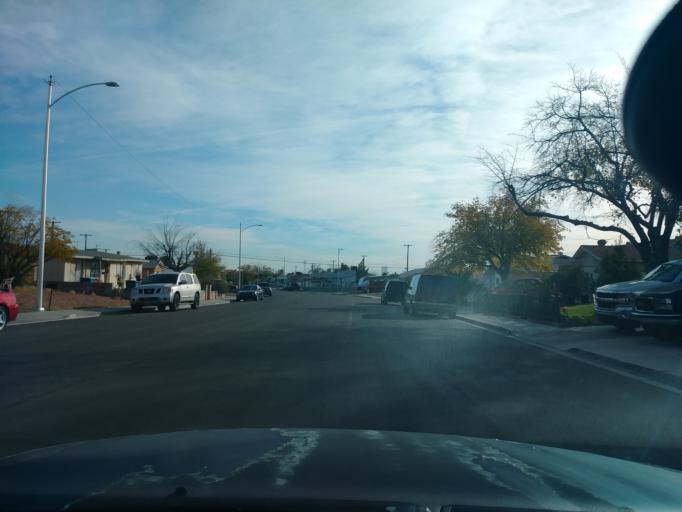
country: US
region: Nevada
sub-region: Clark County
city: Spring Valley
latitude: 36.1624
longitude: -115.2378
